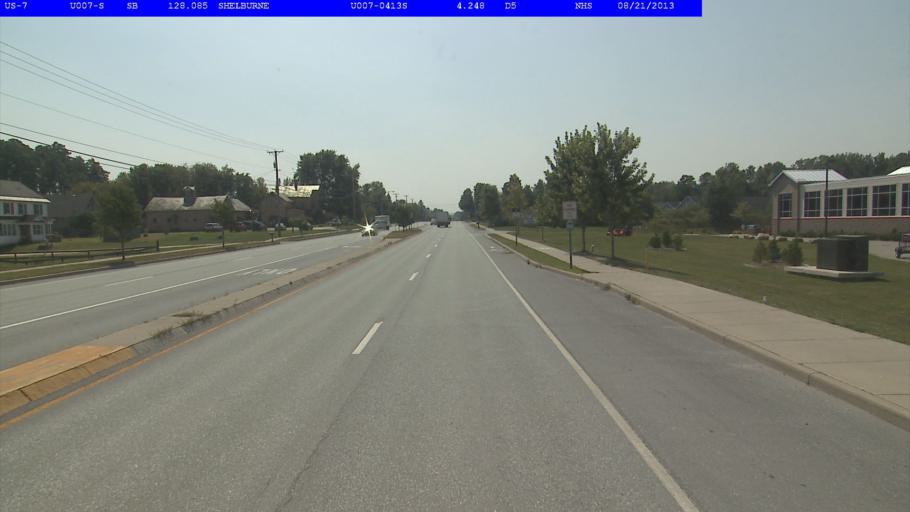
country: US
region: Vermont
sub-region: Chittenden County
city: Burlington
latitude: 44.4030
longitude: -73.2178
